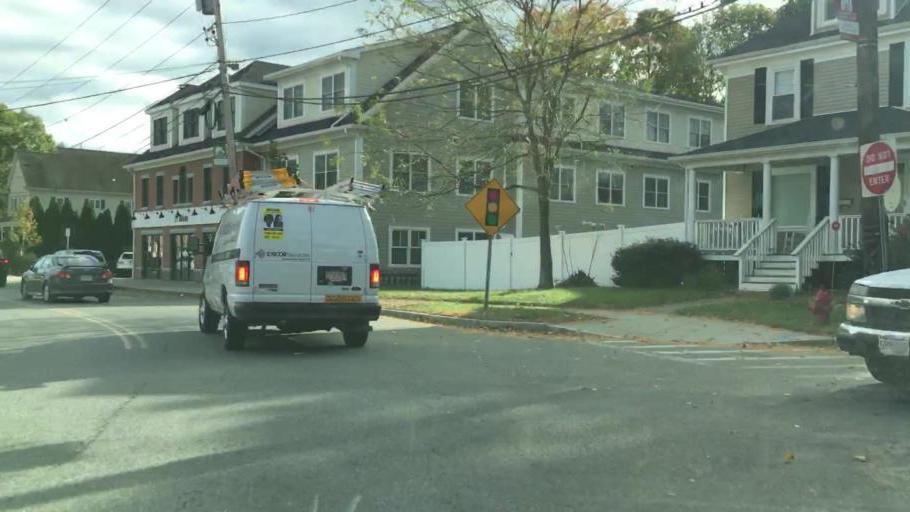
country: US
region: Massachusetts
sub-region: Middlesex County
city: Ashland
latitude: 42.2630
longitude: -71.4673
